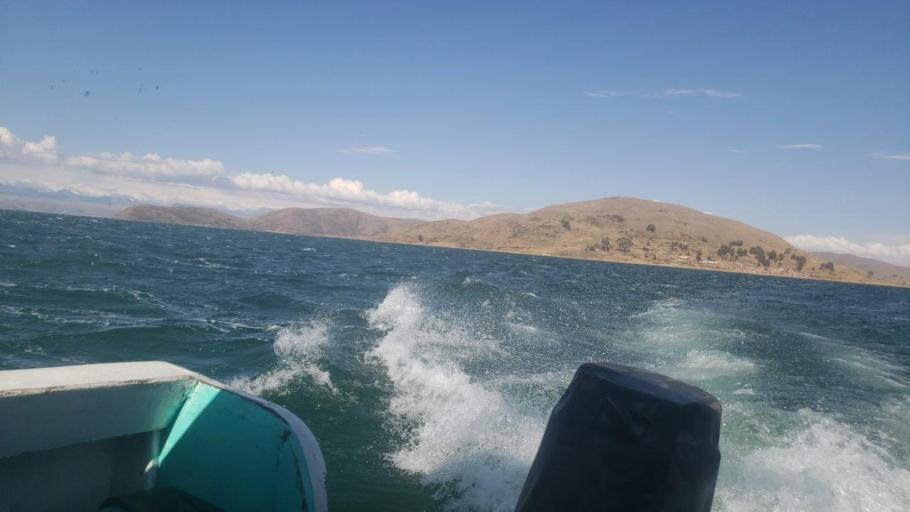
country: BO
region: La Paz
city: Huatajata
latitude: -16.3225
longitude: -68.7312
